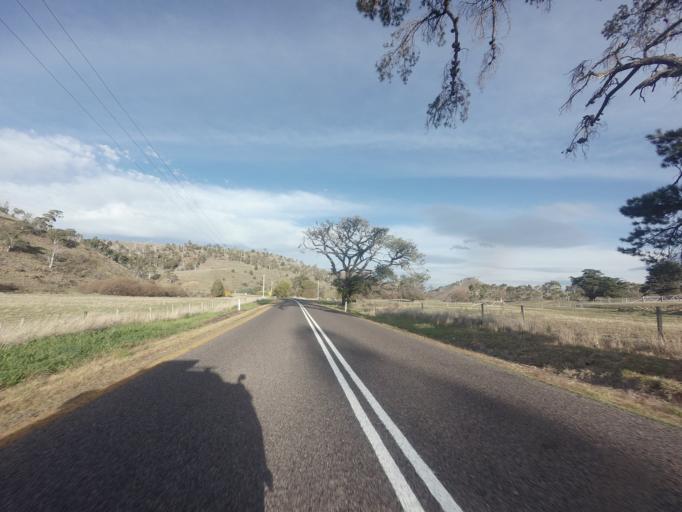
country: AU
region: Tasmania
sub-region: Brighton
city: Bridgewater
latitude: -42.4366
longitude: 147.1475
